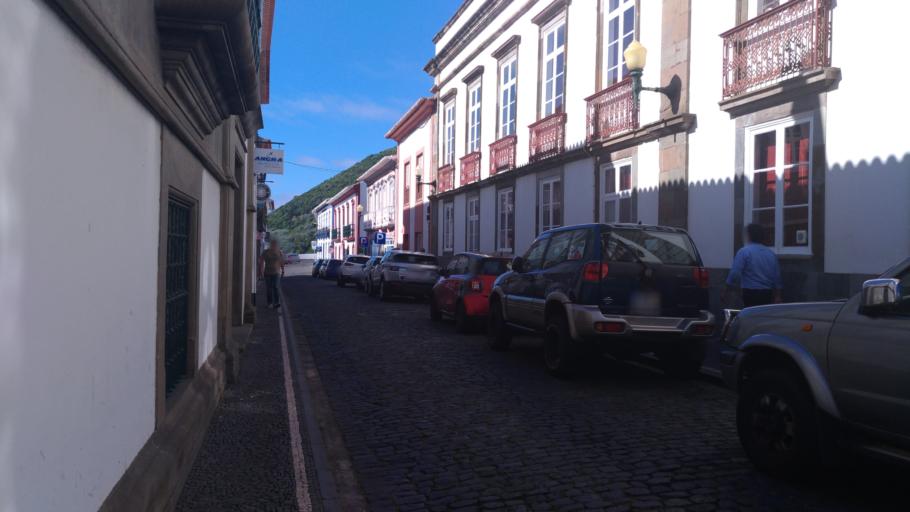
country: PT
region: Azores
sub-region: Angra do Heroismo
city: Angra do Heroismo
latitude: 38.6546
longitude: -27.2212
